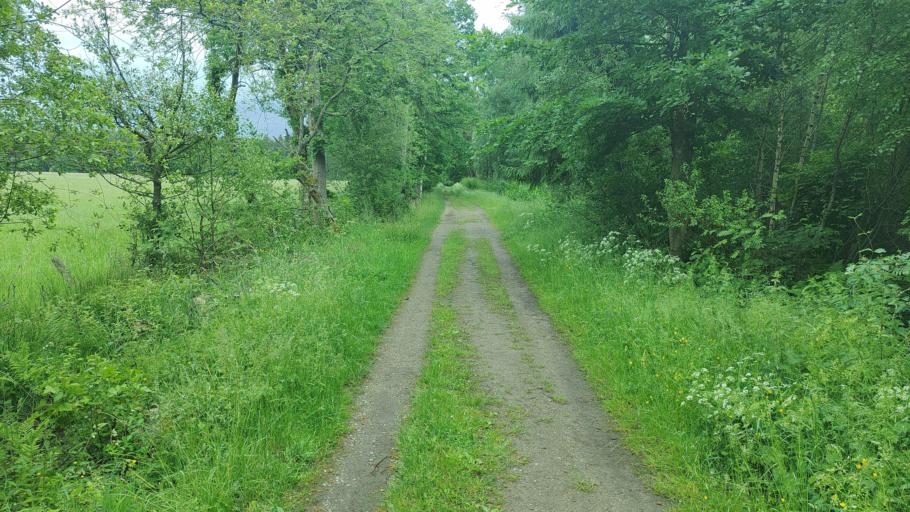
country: DE
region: North Rhine-Westphalia
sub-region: Regierungsbezirk Koln
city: Roetgen
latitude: 50.6251
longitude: 6.1780
